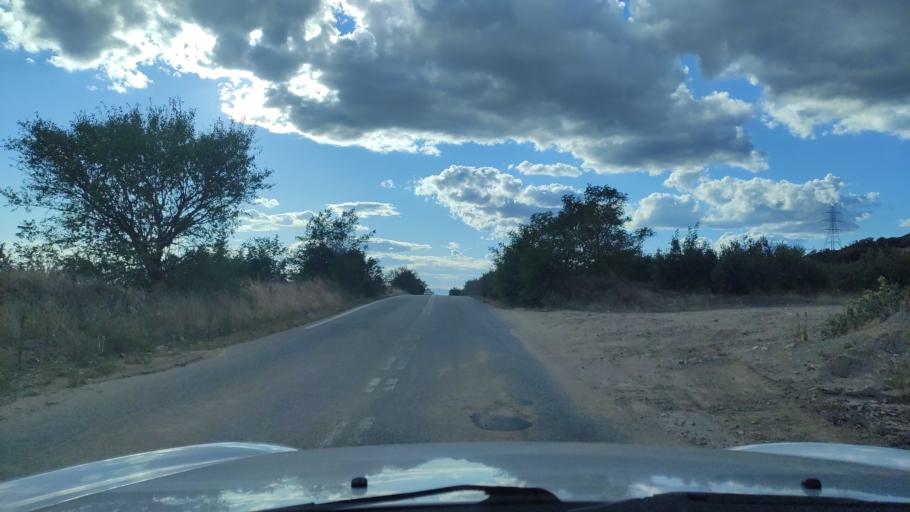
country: GR
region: East Macedonia and Thrace
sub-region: Nomos Rodopis
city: Iasmos
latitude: 41.1189
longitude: 25.1134
